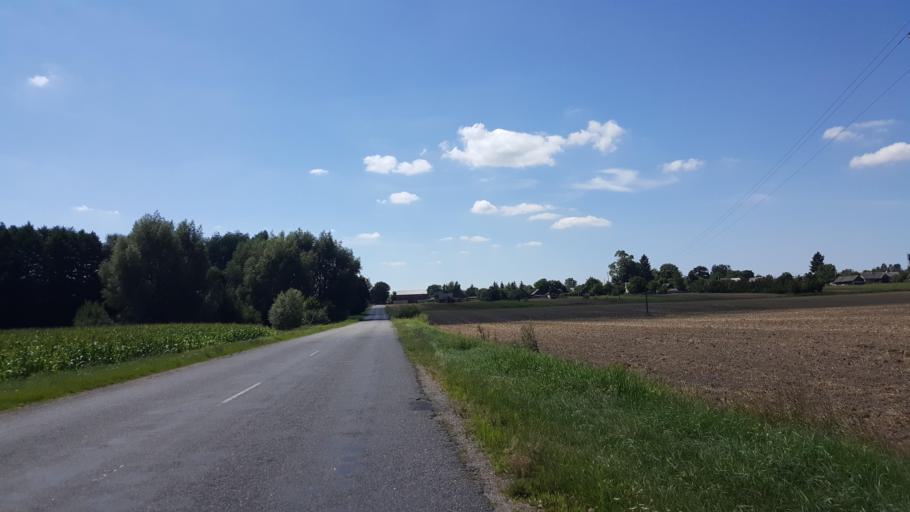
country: BY
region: Brest
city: Charnawchytsy
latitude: 52.3487
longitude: 23.6149
